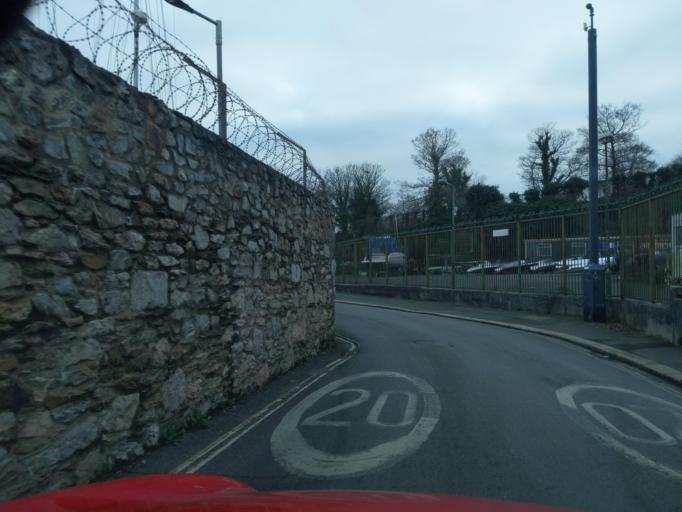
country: GB
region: England
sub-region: Cornwall
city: Millbrook
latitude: 50.3664
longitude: -4.1675
